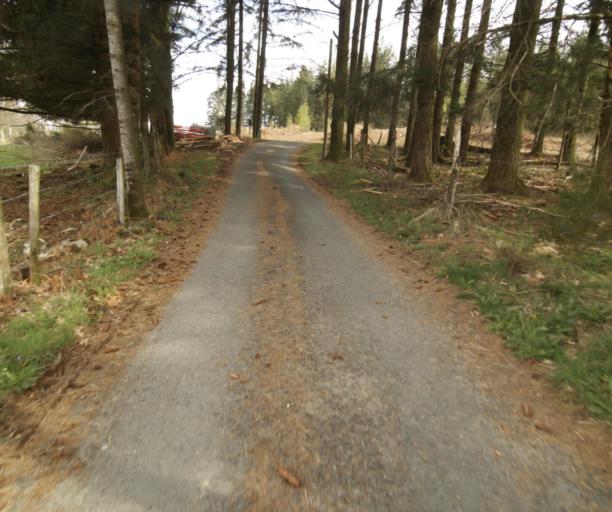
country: FR
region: Limousin
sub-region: Departement de la Correze
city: Correze
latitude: 45.3900
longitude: 1.9134
